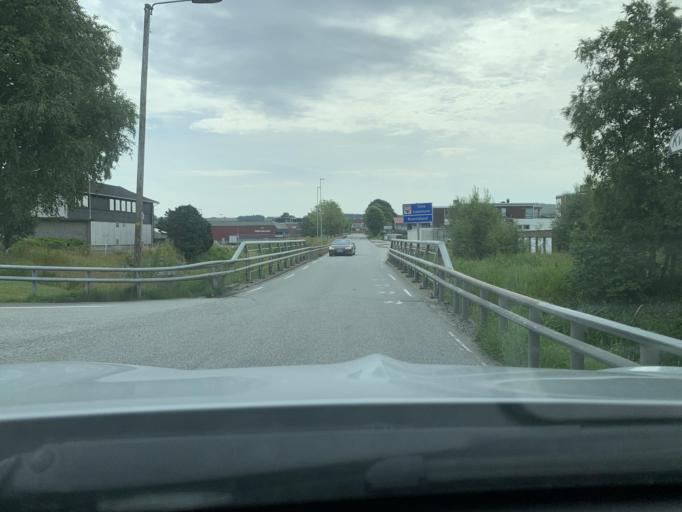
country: NO
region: Rogaland
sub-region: Sandnes
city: Sandnes
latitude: 58.7831
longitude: 5.7151
